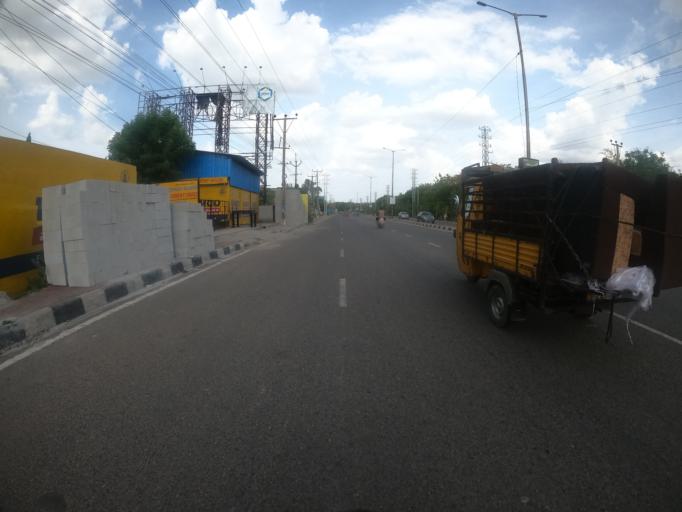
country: IN
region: Telangana
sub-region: Hyderabad
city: Hyderabad
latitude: 17.3511
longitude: 78.3670
